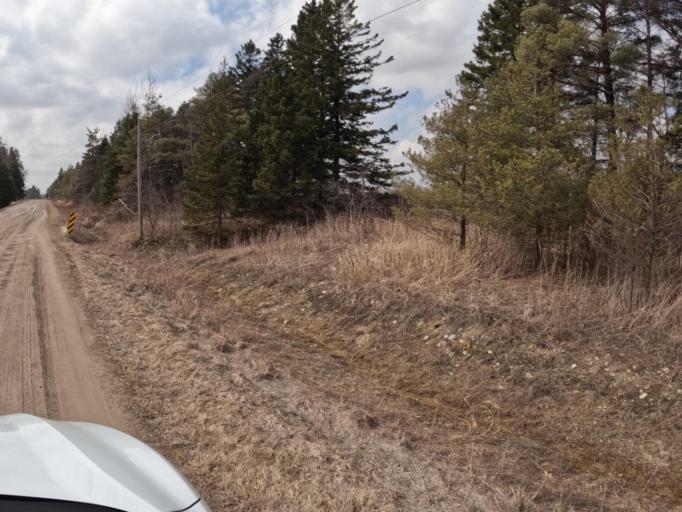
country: CA
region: Ontario
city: Shelburne
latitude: 44.0243
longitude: -80.2801
